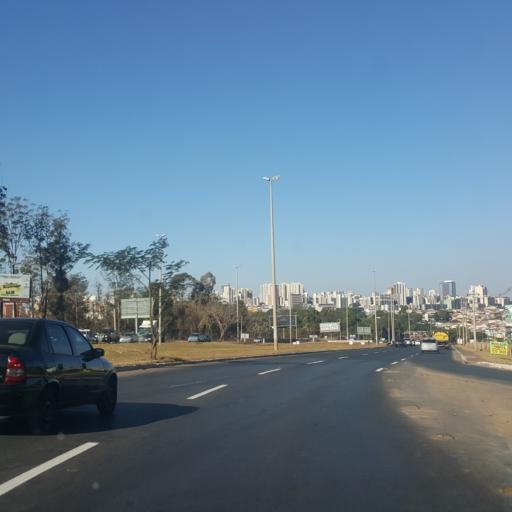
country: BR
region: Federal District
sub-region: Brasilia
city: Brasilia
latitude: -15.8352
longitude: -48.0734
